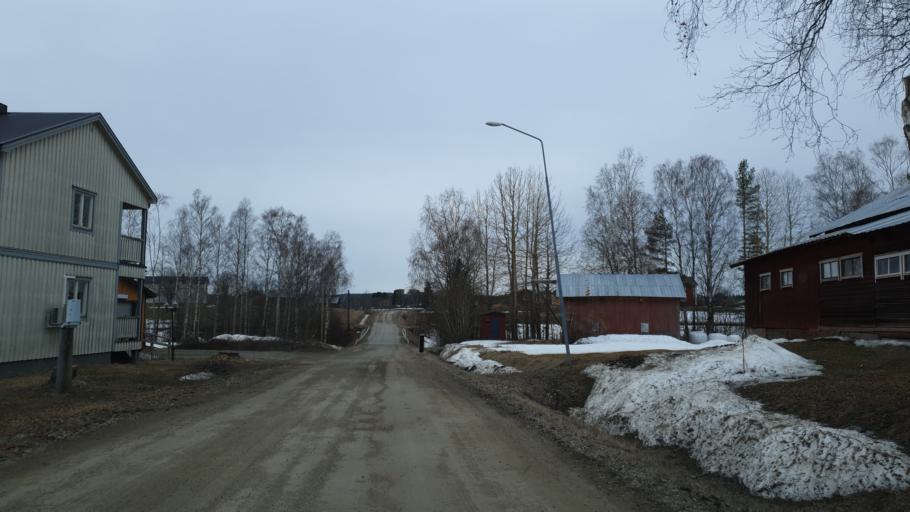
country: SE
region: Vaesterbotten
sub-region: Robertsfors Kommun
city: Robertsfors
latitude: 64.3819
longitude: 20.9185
